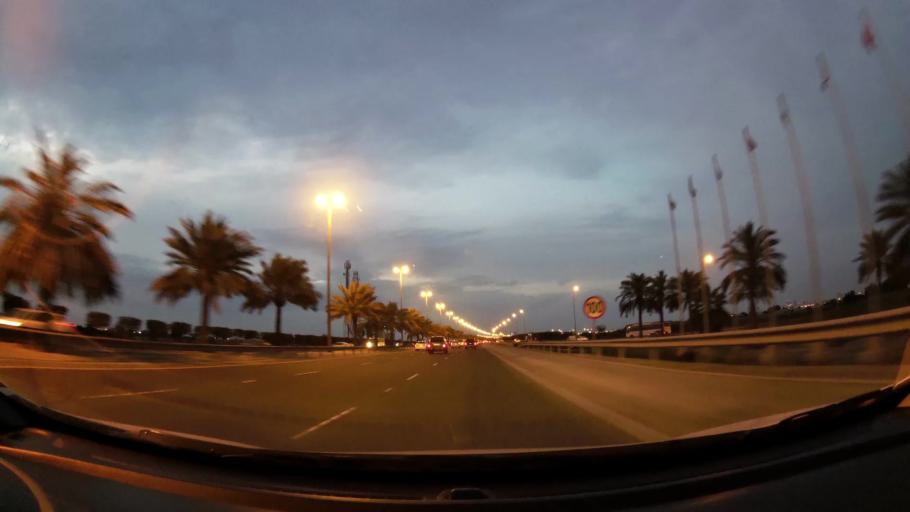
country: BH
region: Northern
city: Madinat `Isa
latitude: 26.1648
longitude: 50.5038
